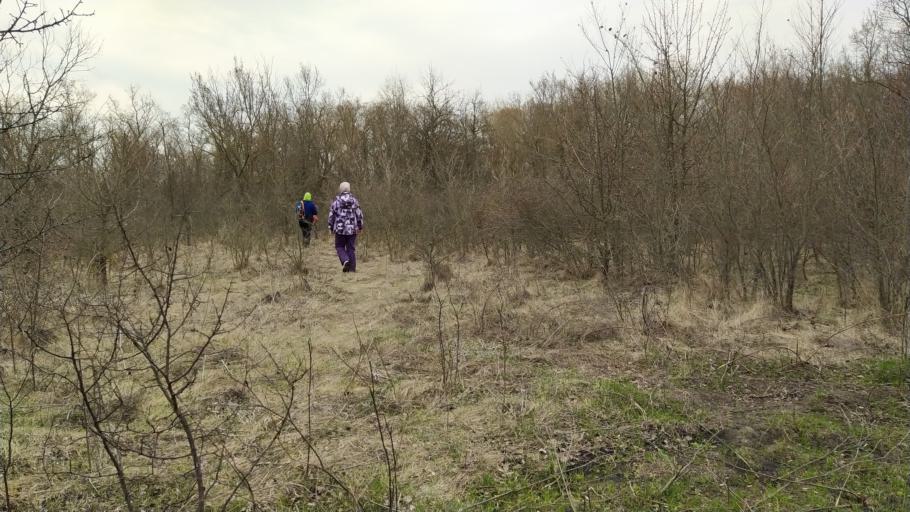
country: RU
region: Rostov
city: Semikarakorsk
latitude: 47.5395
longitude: 40.6813
